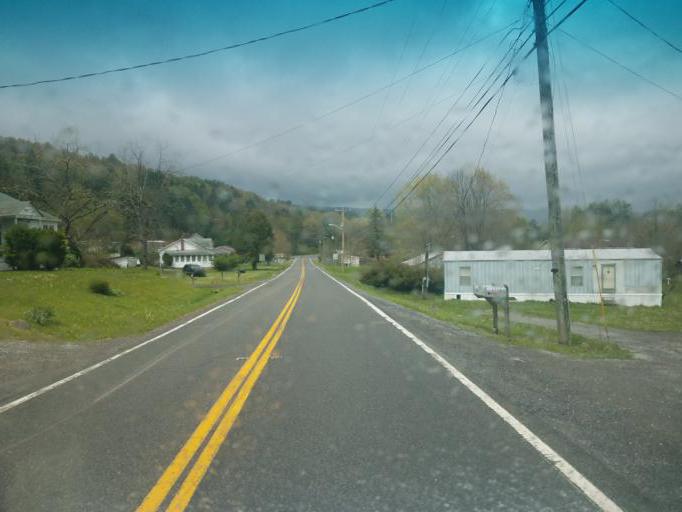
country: US
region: Virginia
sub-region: Bland County
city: Bland
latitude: 37.1578
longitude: -81.1497
